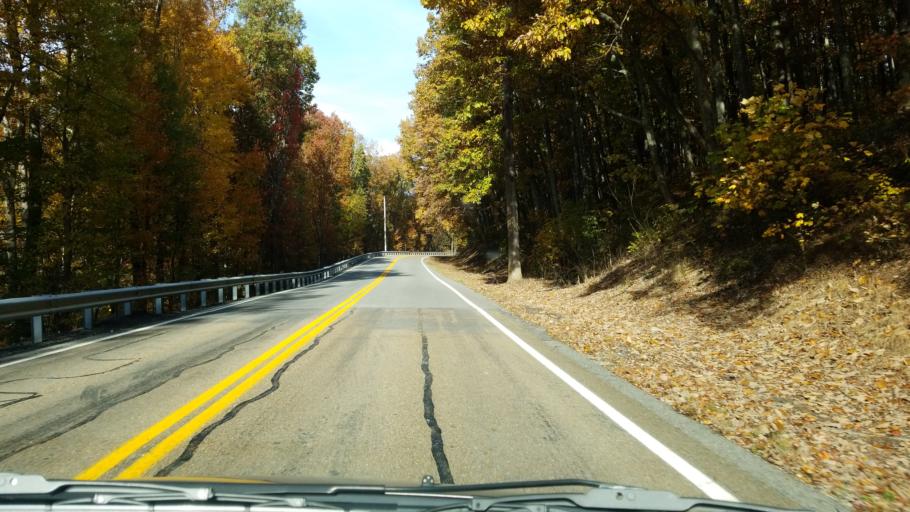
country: US
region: Tennessee
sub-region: Grundy County
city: Gruetli-Laager
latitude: 35.4407
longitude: -85.5203
